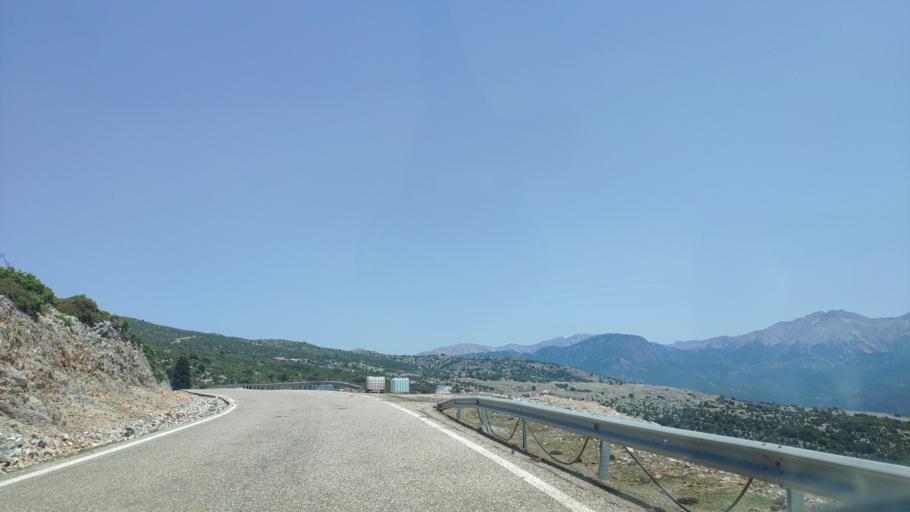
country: GR
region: West Greece
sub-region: Nomos Aitolias kai Akarnanias
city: Krikellos
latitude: 39.0652
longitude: 21.3820
